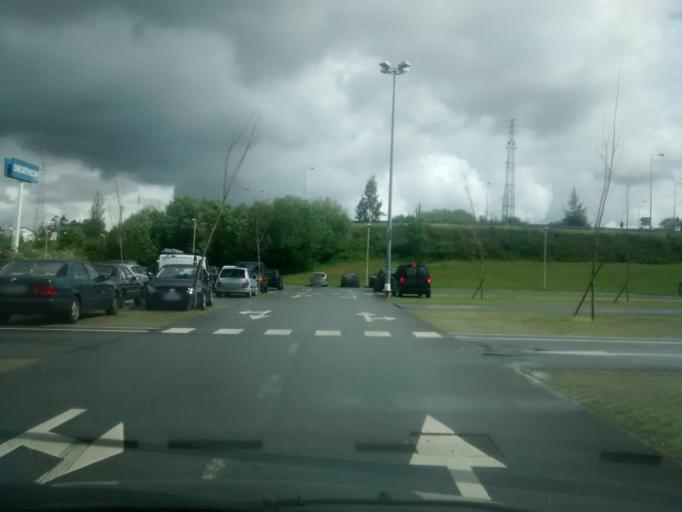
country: PT
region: Braga
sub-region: Braga
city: Braga
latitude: 41.5698
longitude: -8.4280
